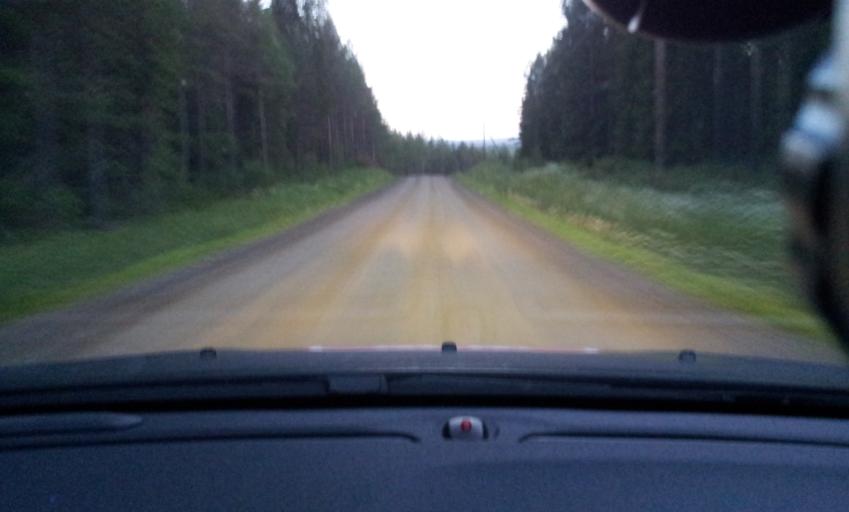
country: SE
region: Vaesternorrland
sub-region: Ange Kommun
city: Ange
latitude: 62.7685
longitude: 15.8086
